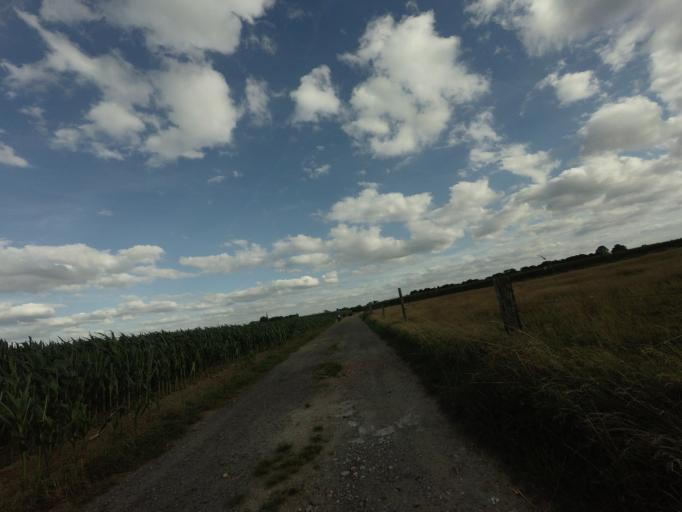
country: BE
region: Flanders
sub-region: Provincie Vlaams-Brabant
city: Grimbergen
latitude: 50.9725
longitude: 4.3726
